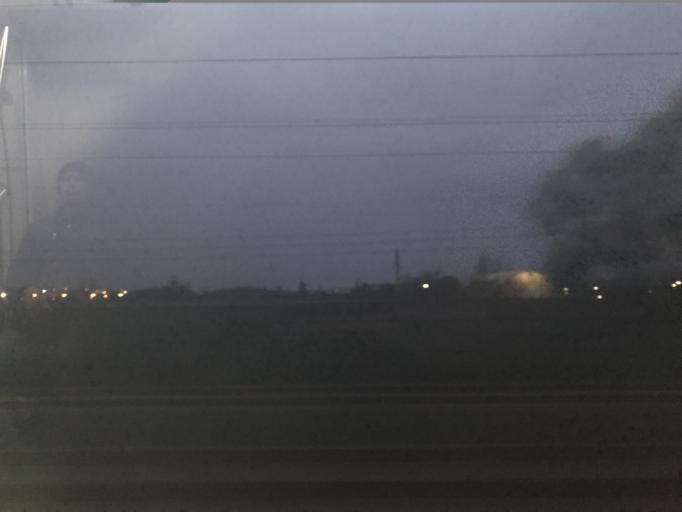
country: TR
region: Kocaeli
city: Darica
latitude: 40.8096
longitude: 29.3534
